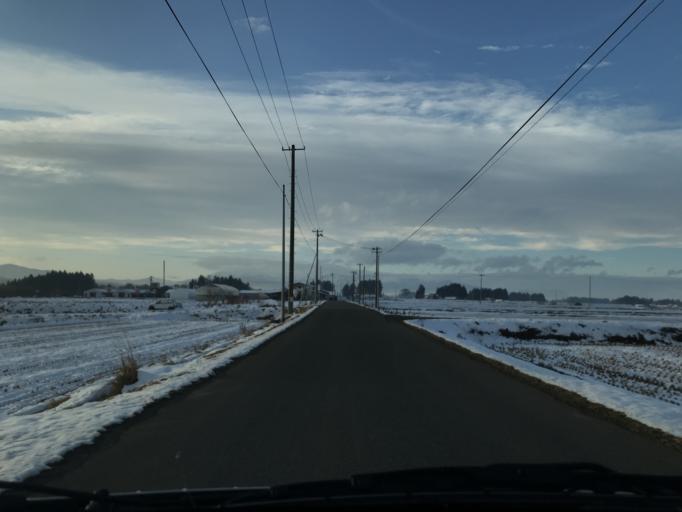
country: JP
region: Iwate
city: Mizusawa
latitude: 39.0516
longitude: 141.0996
